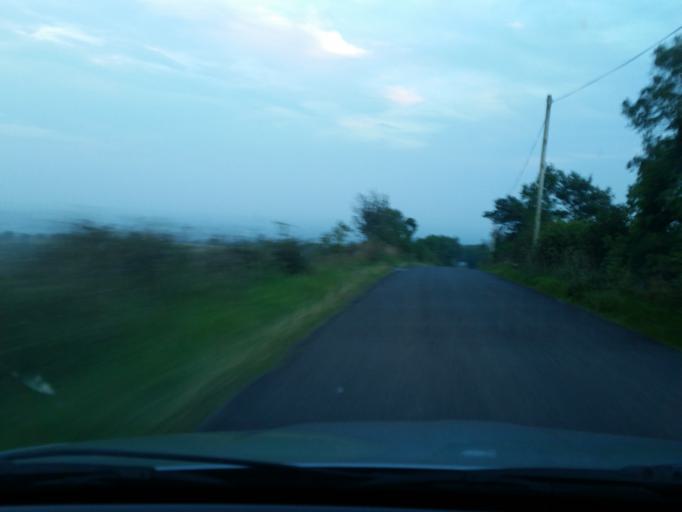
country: IE
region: Ulster
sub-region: County Monaghan
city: Clones
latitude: 54.2630
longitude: -7.2750
